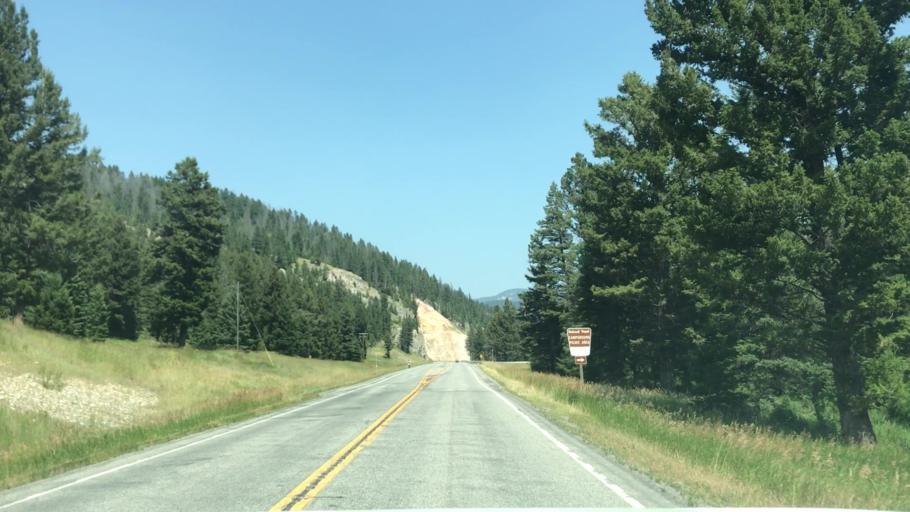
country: US
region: Montana
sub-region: Gallatin County
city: Big Sky
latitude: 45.1723
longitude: -111.2435
